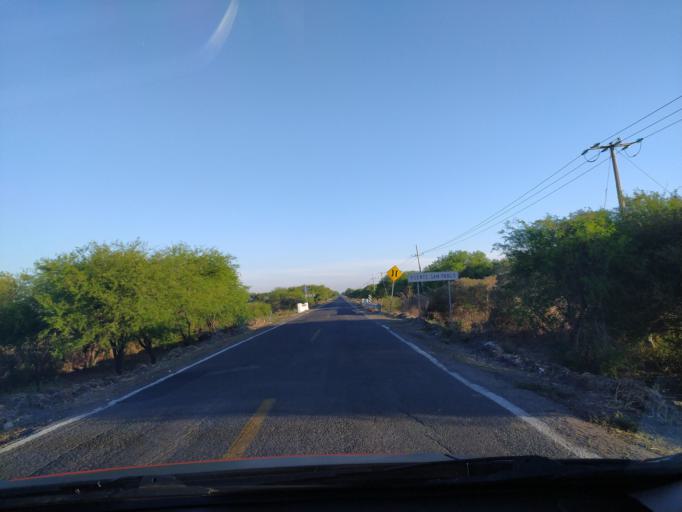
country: MX
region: Guanajuato
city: Ciudad Manuel Doblado
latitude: 20.7529
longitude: -101.8256
